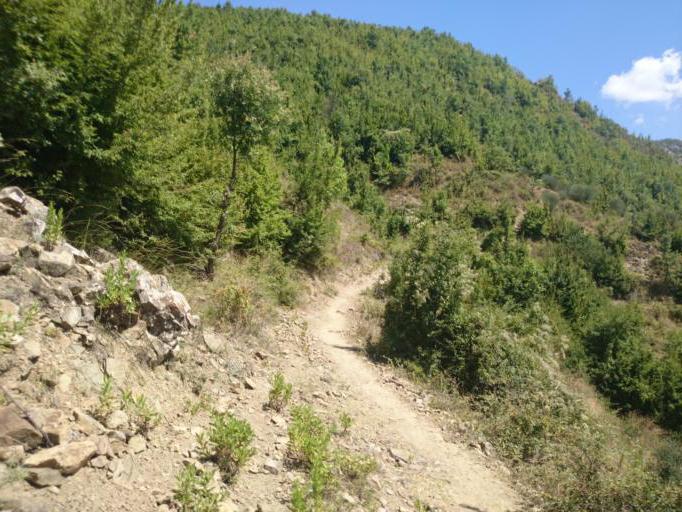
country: AL
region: Elbasan
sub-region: Rrethi i Elbasanit
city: Shushice
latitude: 41.0609
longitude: 20.1386
